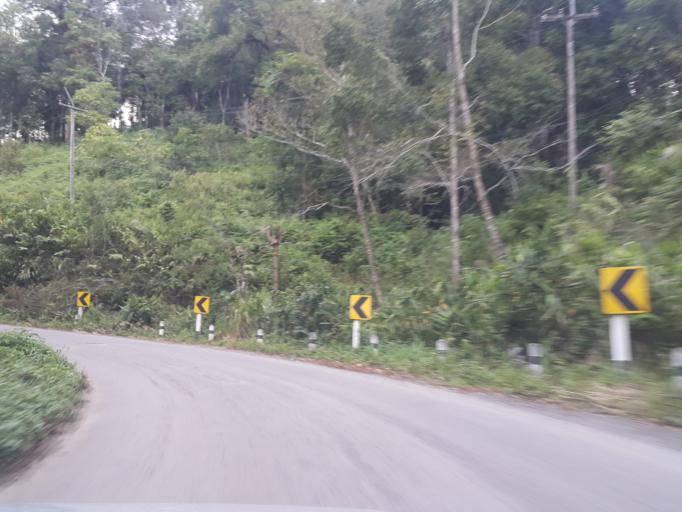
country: TH
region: Mae Hong Son
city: Khun Yuam
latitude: 18.7966
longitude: 98.0921
